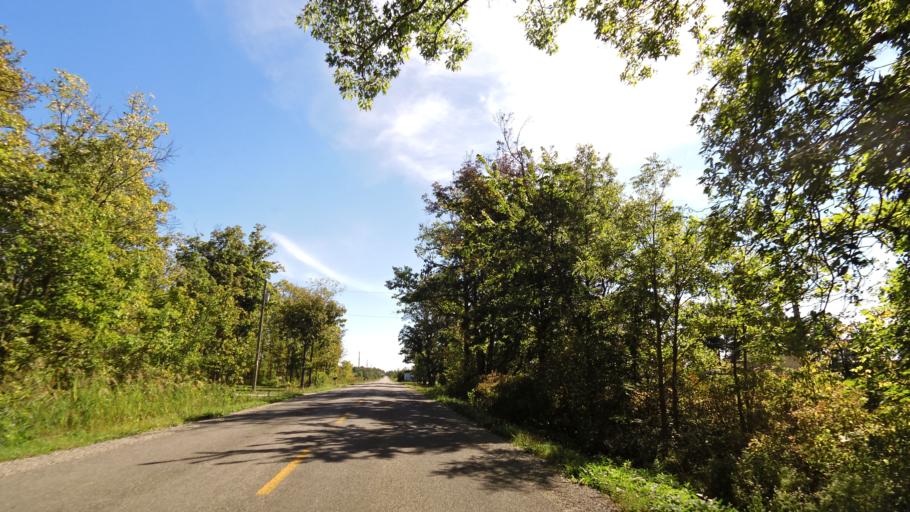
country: CA
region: Ontario
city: Brantford
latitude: 43.0894
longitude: -80.1175
